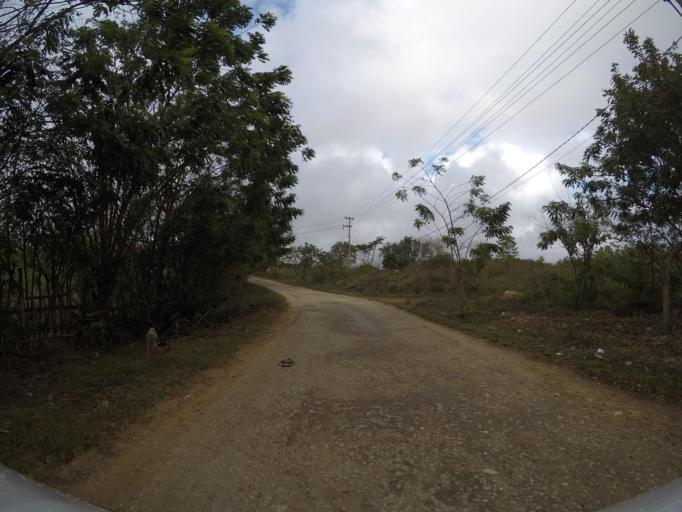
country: TL
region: Lautem
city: Lospalos
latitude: -8.5267
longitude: 126.9864
